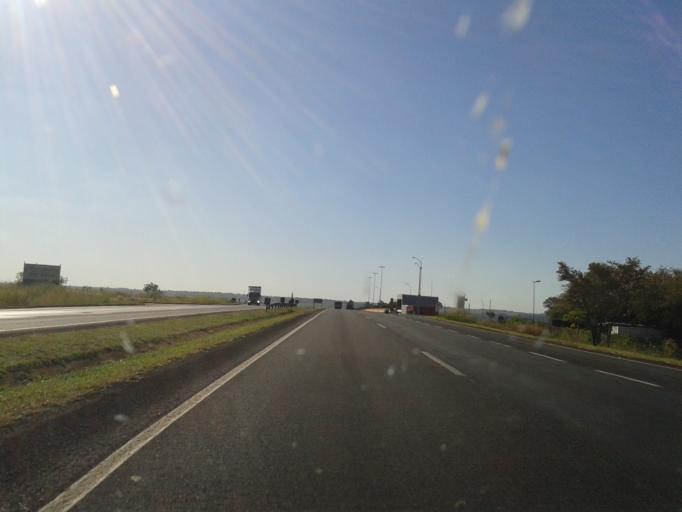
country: BR
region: Minas Gerais
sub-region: Uberlandia
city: Uberlandia
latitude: -19.0237
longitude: -48.2043
